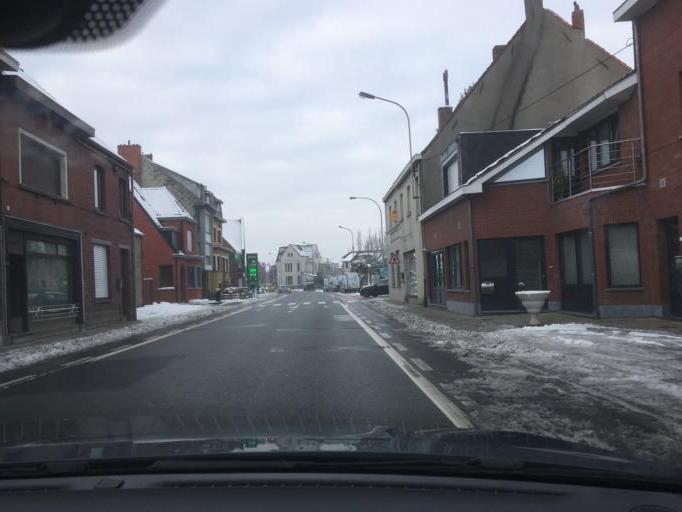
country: BE
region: Flanders
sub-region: Provincie West-Vlaanderen
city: Kortrijk
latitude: 50.8373
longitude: 3.2430
